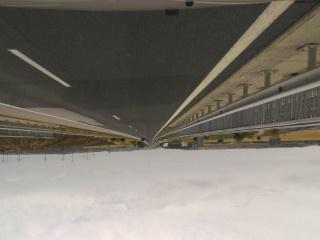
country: BG
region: Stara Zagora
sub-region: Obshtina Chirpan
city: Chirpan
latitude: 42.2110
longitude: 25.3108
